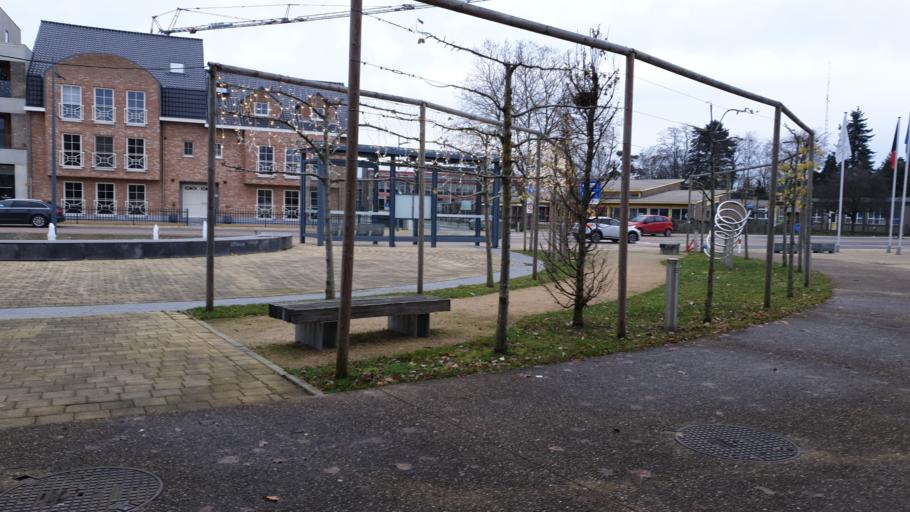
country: BE
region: Flanders
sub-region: Provincie Antwerpen
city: Balen
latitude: 51.1016
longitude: 5.1487
